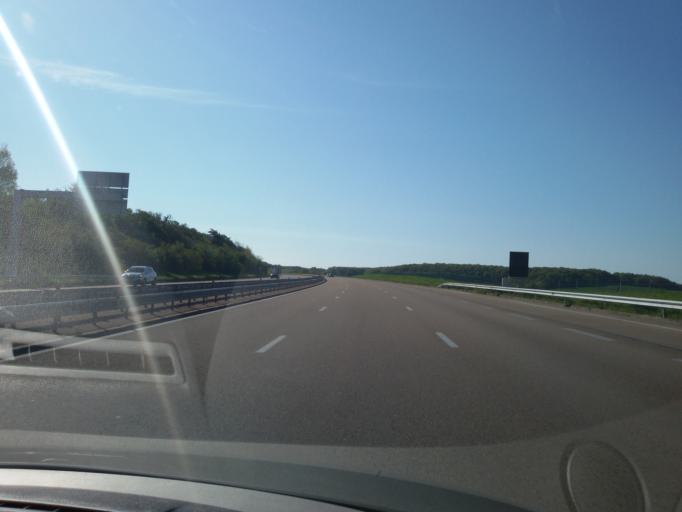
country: FR
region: Bourgogne
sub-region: Departement de l'Yonne
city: Saint-Julien-du-Sault
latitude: 47.9339
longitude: 3.2483
